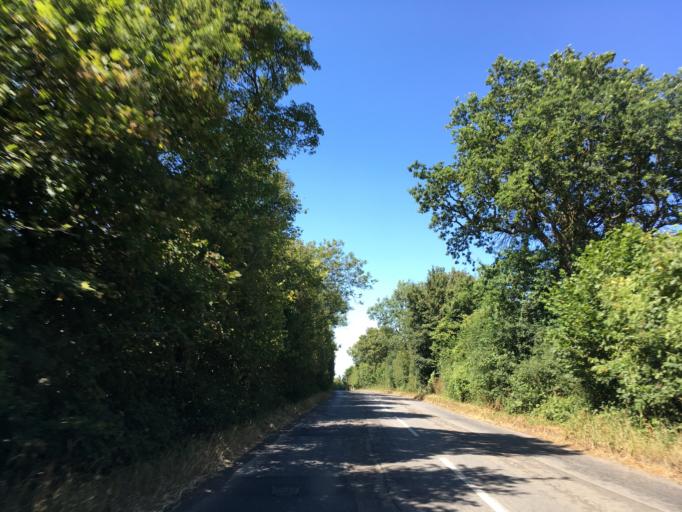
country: GB
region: England
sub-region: South Gloucestershire
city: Chipping Sodbury
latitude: 51.5214
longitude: -2.3950
